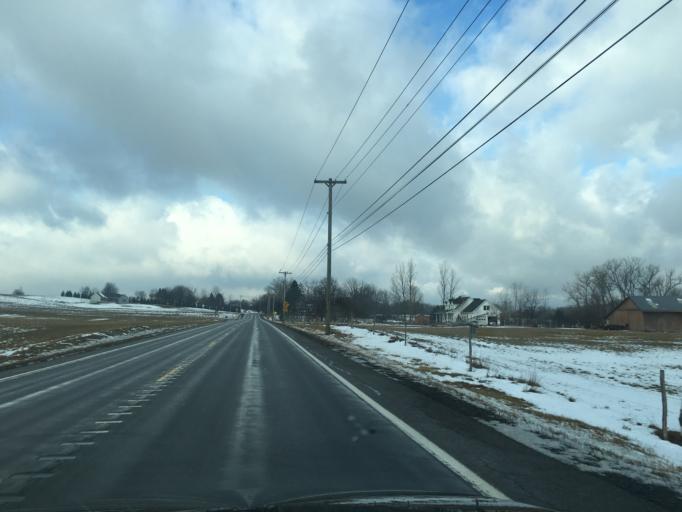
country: US
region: New York
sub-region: Ontario County
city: Manchester
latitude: 42.9671
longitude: -77.2883
